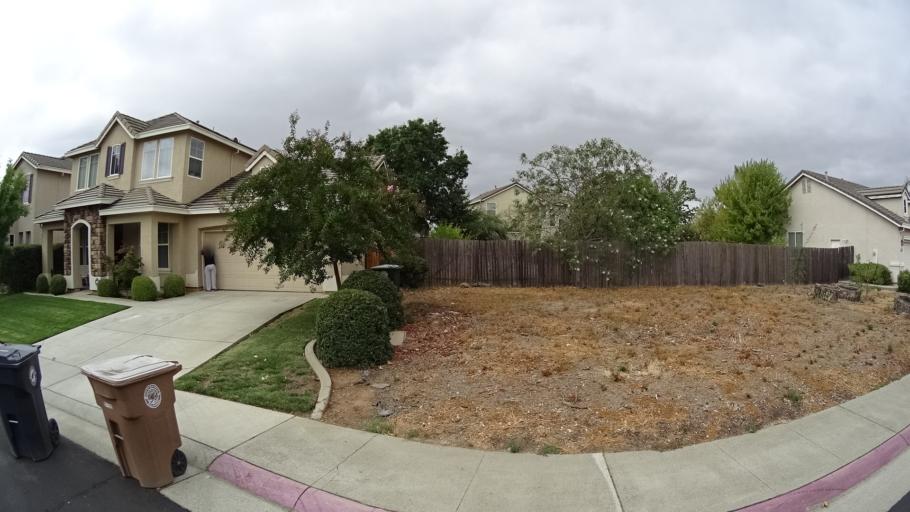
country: US
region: California
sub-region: Sacramento County
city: Laguna
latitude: 38.4149
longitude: -121.4505
